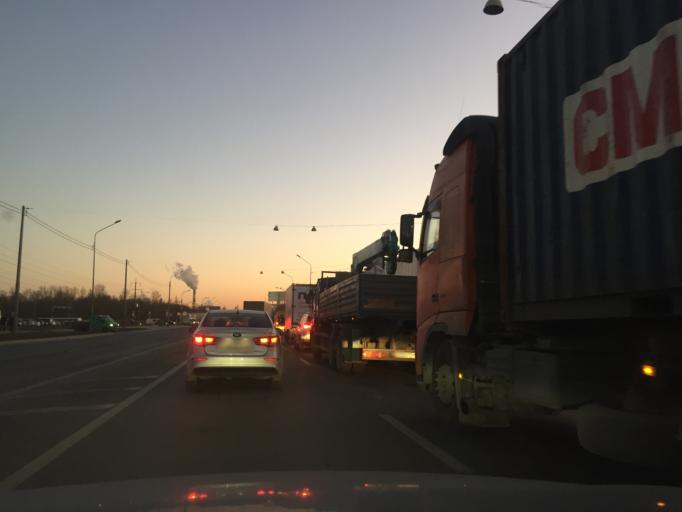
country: RU
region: St.-Petersburg
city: Obukhovo
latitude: 59.8537
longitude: 30.4250
